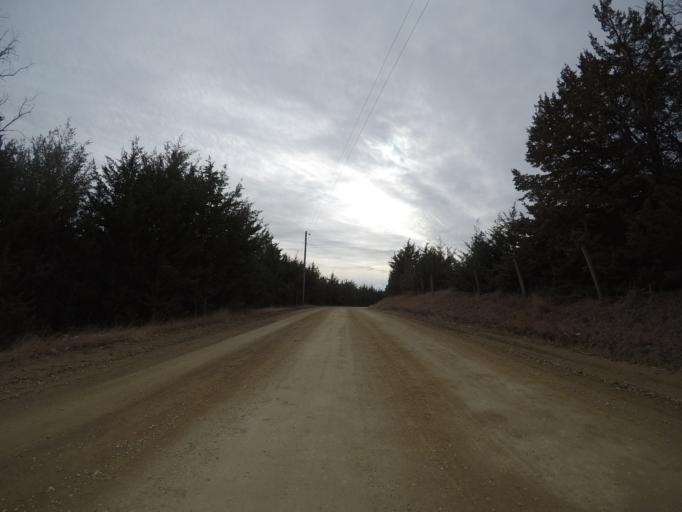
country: US
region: Kansas
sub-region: Riley County
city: Ogden
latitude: 39.1743
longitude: -96.6783
